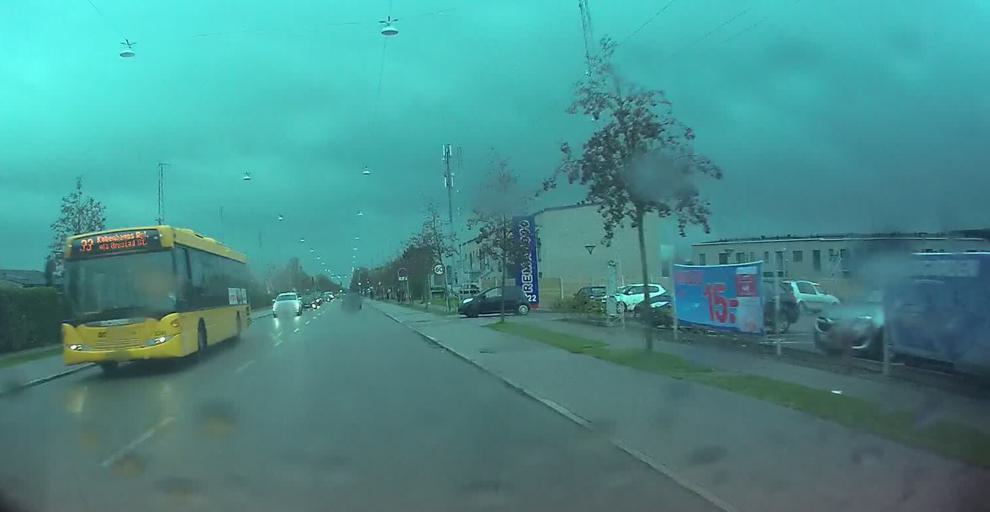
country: DK
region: Capital Region
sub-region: Tarnby Kommune
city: Tarnby
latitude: 55.6101
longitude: 12.5845
